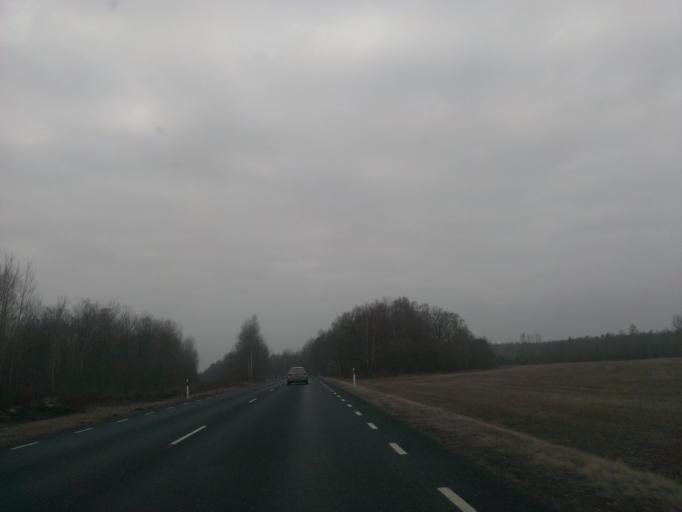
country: EE
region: Saare
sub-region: Orissaare vald
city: Orissaare
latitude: 58.6062
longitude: 23.2948
